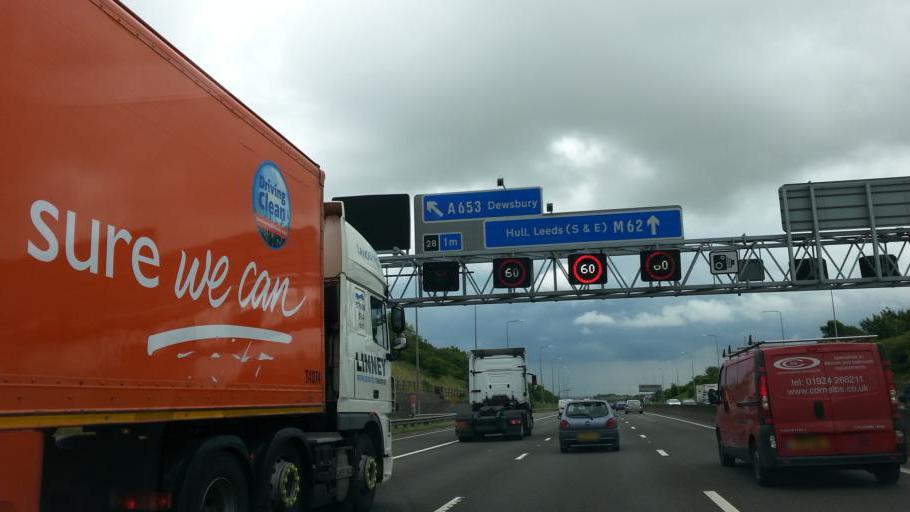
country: GB
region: England
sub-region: City and Borough of Leeds
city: Morley
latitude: 53.7327
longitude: -1.6109
